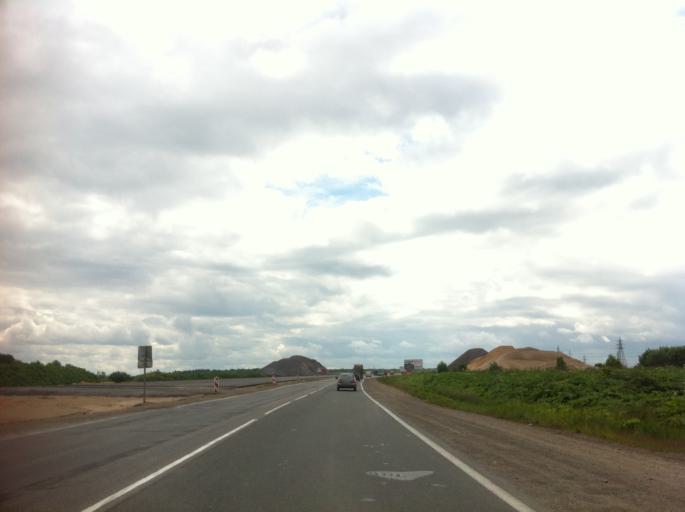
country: RU
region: Leningrad
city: Gatchina
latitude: 59.5437
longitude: 30.1634
